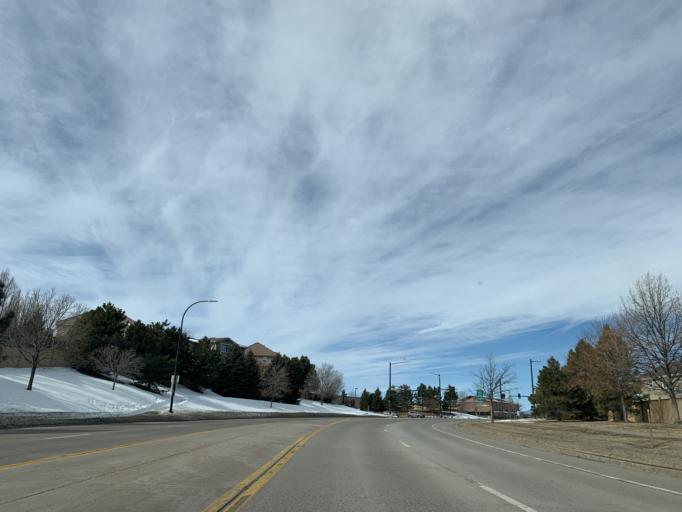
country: US
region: Colorado
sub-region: Douglas County
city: Carriage Club
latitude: 39.5255
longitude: -104.9370
